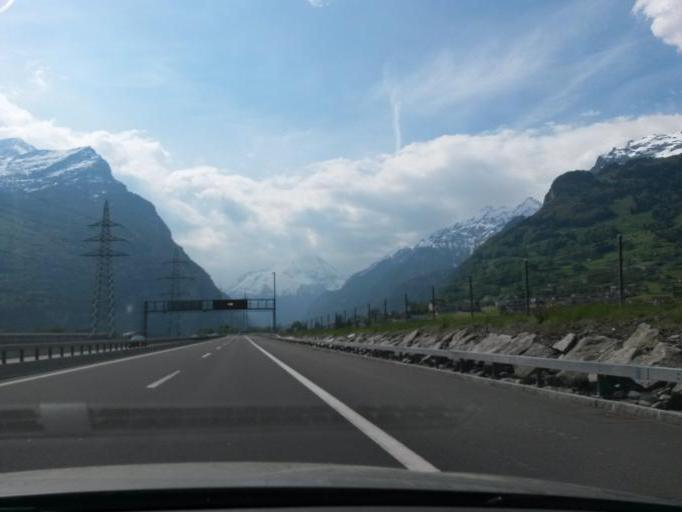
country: CH
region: Uri
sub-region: Uri
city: Attinghausen
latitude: 46.8703
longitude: 8.6293
